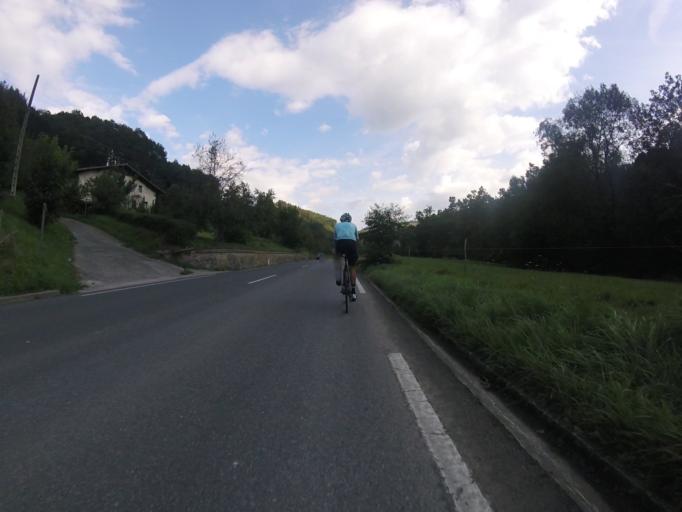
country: ES
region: Basque Country
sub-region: Provincia de Guipuzcoa
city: Amezqueta
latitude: 43.0586
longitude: -2.0878
